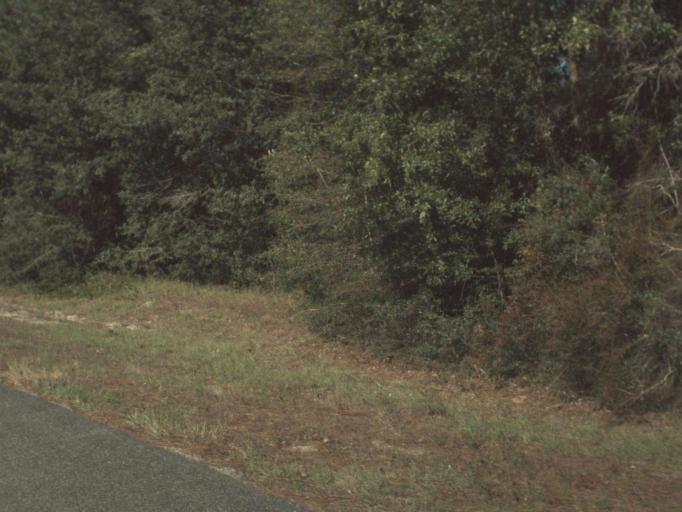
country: US
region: Florida
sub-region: Okaloosa County
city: Crestview
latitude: 30.8253
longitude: -86.7246
